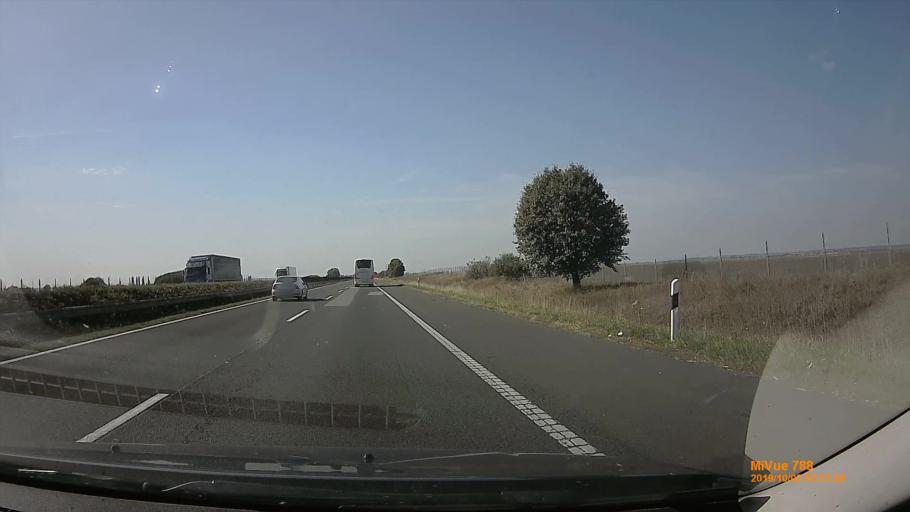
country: HU
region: Pest
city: Galgaheviz
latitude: 47.6598
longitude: 19.5928
